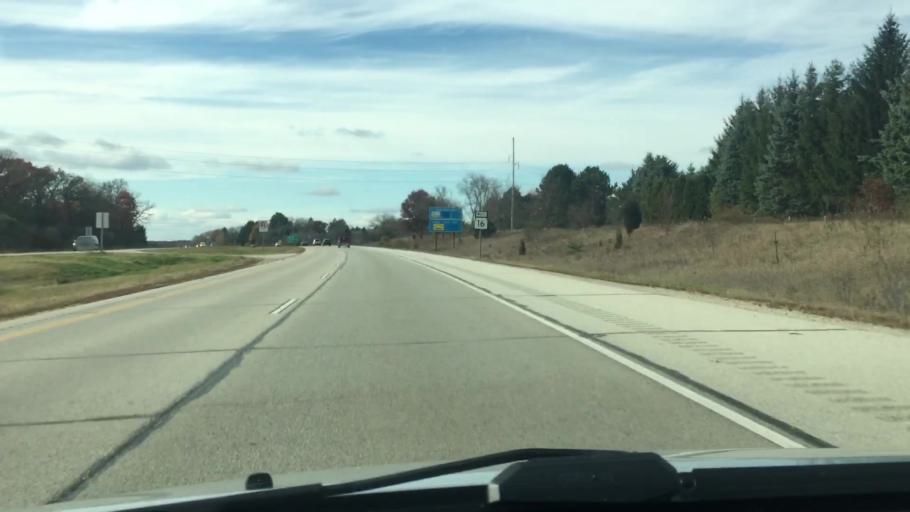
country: US
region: Wisconsin
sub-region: Waukesha County
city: Hartland
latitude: 43.1085
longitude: -88.3214
